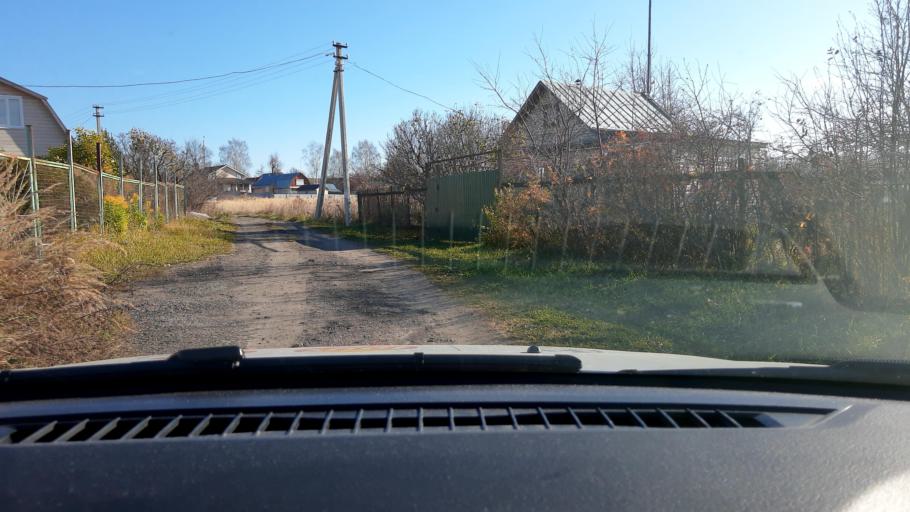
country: RU
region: Nizjnij Novgorod
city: Dal'neye Konstantinovo
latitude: 55.9666
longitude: 43.9766
